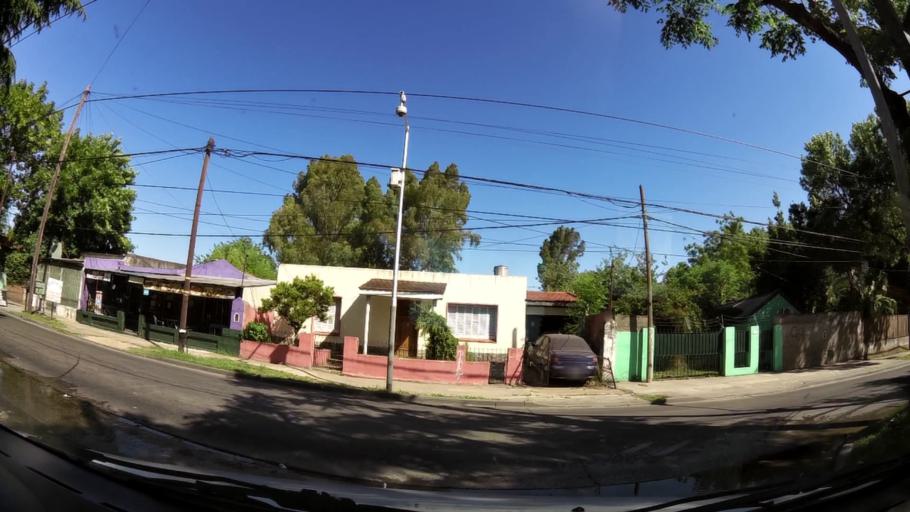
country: AR
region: Buenos Aires
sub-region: Partido de San Isidro
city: San Isidro
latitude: -34.4701
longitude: -58.5326
